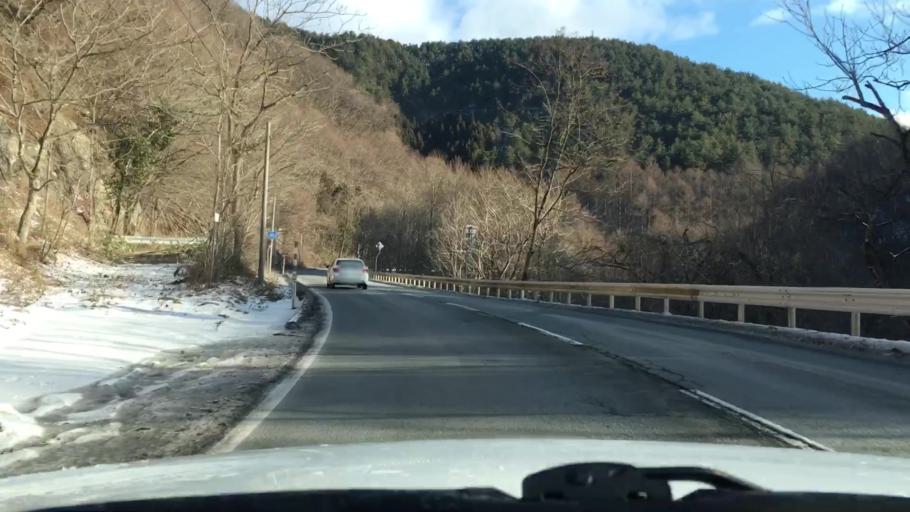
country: JP
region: Iwate
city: Morioka-shi
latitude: 39.6661
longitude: 141.3161
